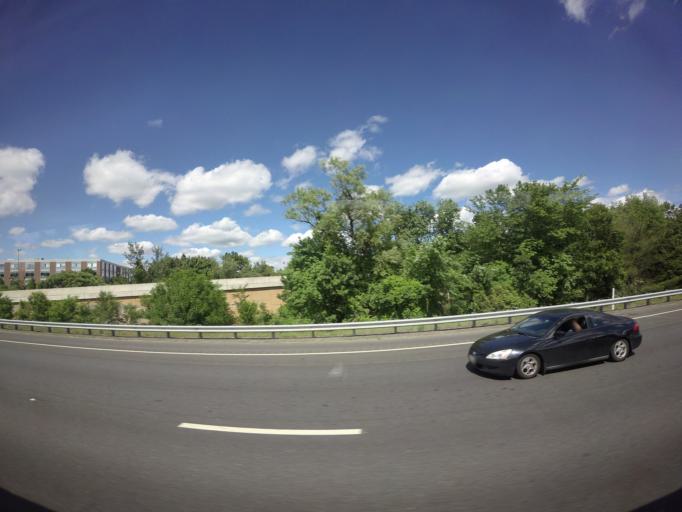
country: US
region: Massachusetts
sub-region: Middlesex County
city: Wilmington
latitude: 42.5852
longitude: -71.1585
